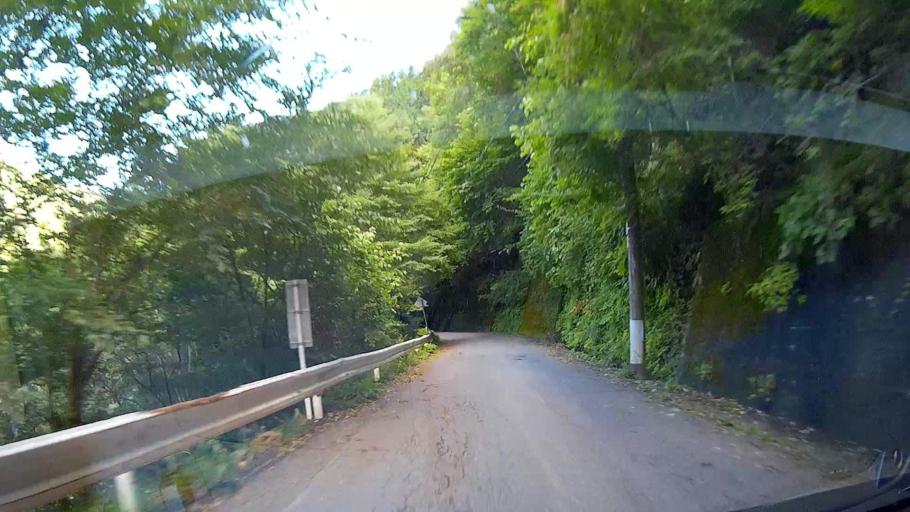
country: JP
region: Shizuoka
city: Shizuoka-shi
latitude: 35.2641
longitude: 138.2263
